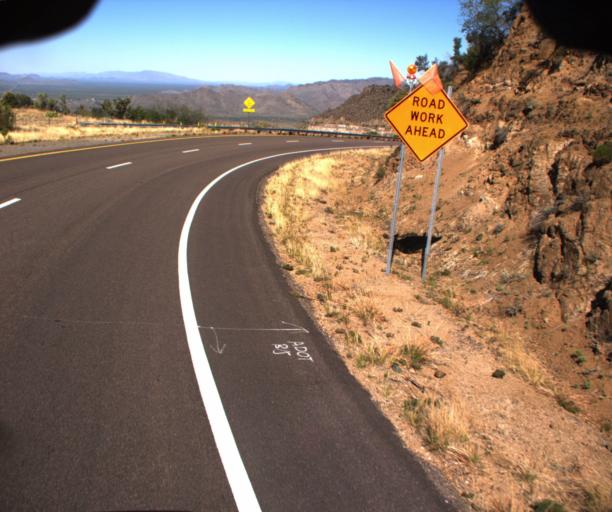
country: US
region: Arizona
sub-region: Yavapai County
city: Congress
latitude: 34.2015
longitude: -112.7630
